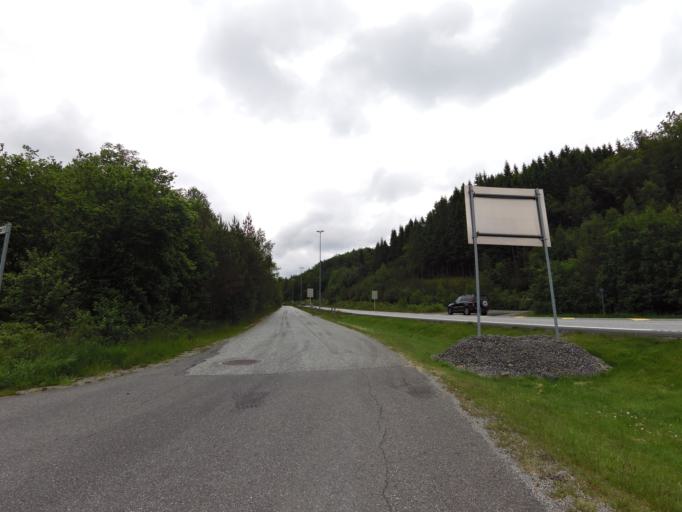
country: NO
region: Vest-Agder
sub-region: Flekkefjord
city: Flekkefjord
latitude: 58.2945
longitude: 6.6912
